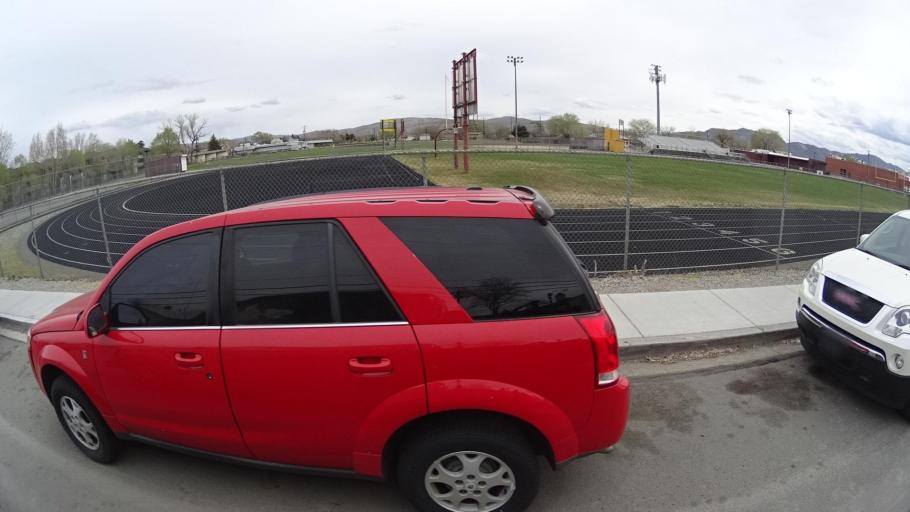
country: US
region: Nevada
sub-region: Washoe County
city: Sparks
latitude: 39.5430
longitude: -119.7620
